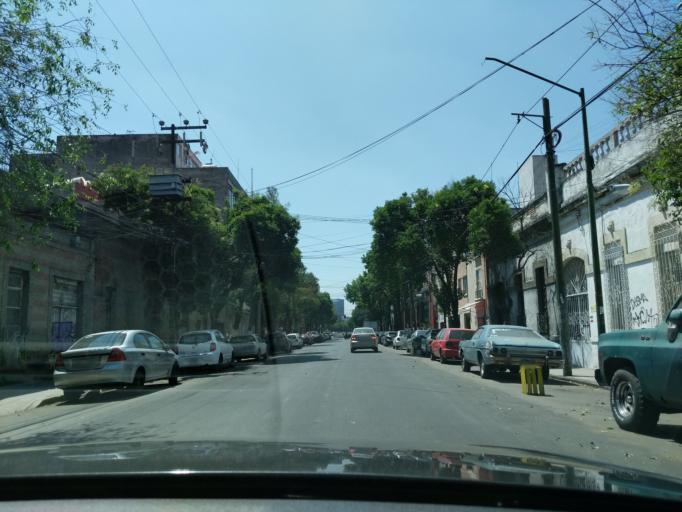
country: MX
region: Mexico City
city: Cuauhtemoc
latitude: 19.4446
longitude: -99.1633
